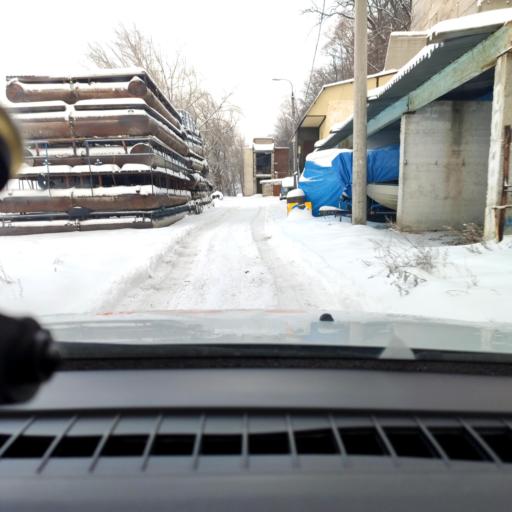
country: RU
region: Samara
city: Samara
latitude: 53.2907
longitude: 50.1920
